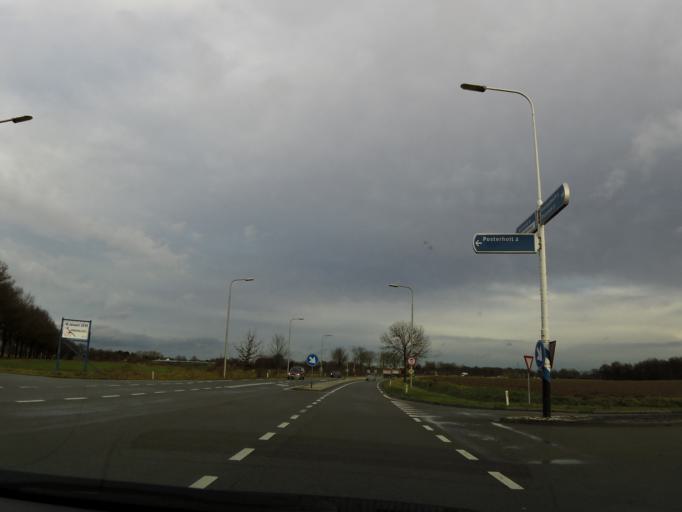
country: NL
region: Limburg
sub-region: Gemeente Roerdalen
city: Posterholt
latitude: 51.1109
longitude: 6.0257
